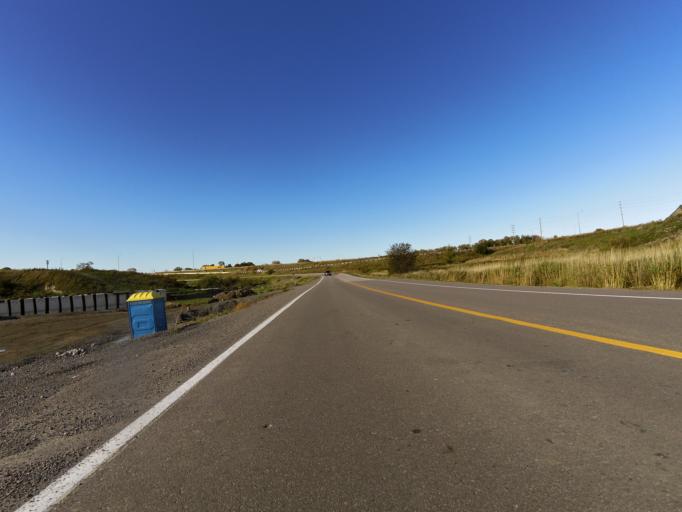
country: CA
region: Ontario
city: Oshawa
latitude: 43.8761
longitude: -78.7643
